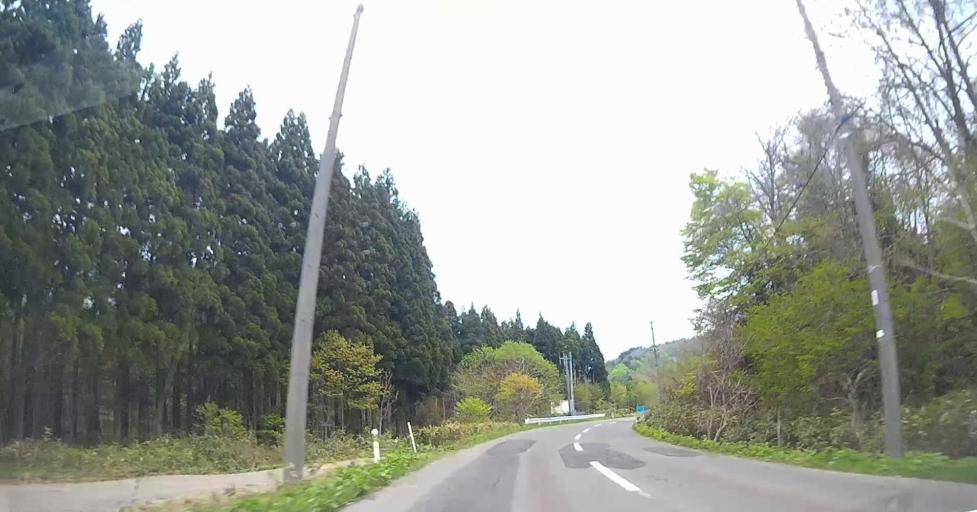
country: JP
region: Aomori
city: Goshogawara
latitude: 41.1211
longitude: 140.5232
